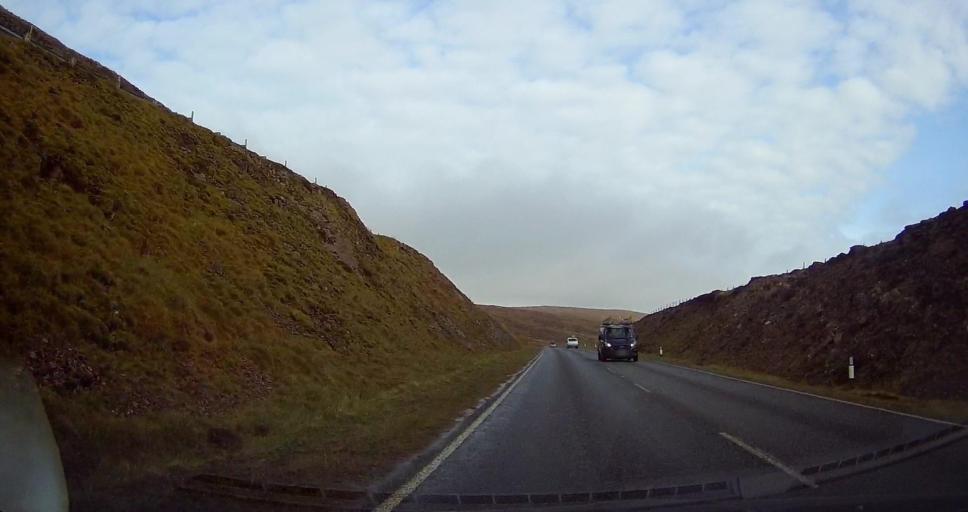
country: GB
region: Scotland
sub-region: Shetland Islands
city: Sandwick
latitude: 60.0676
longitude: -1.2256
